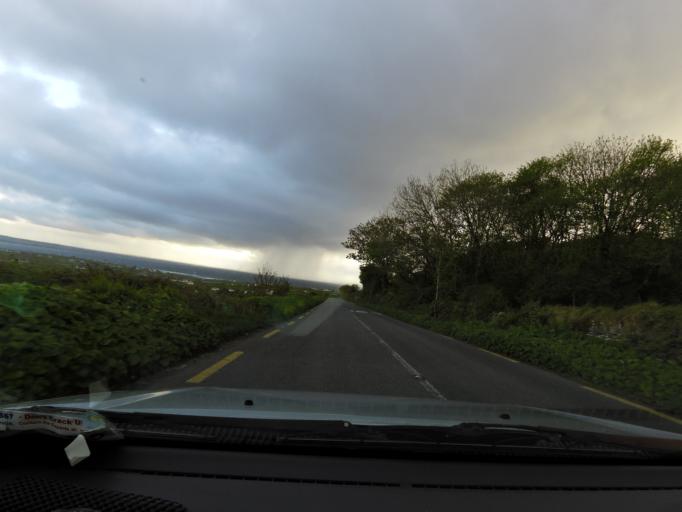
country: IE
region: Munster
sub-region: An Clar
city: Kilrush
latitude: 52.9517
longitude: -9.4225
